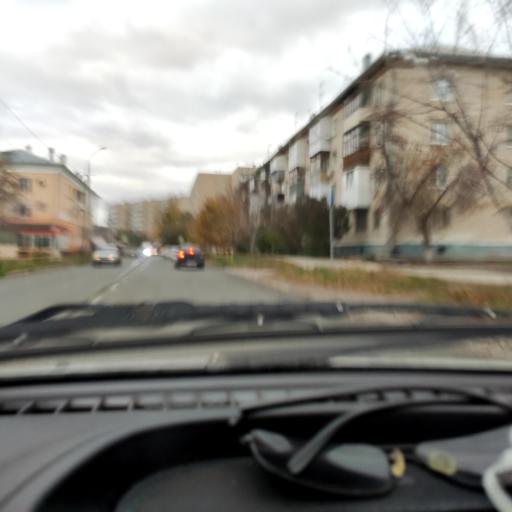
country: RU
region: Samara
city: Tol'yatti
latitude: 53.5052
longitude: 49.3999
